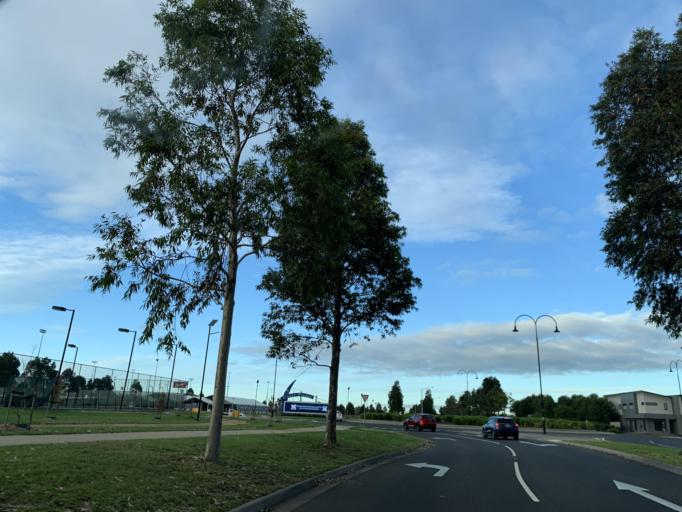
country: AU
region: Victoria
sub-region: Casey
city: Cranbourne East
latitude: -38.1190
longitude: 145.3070
